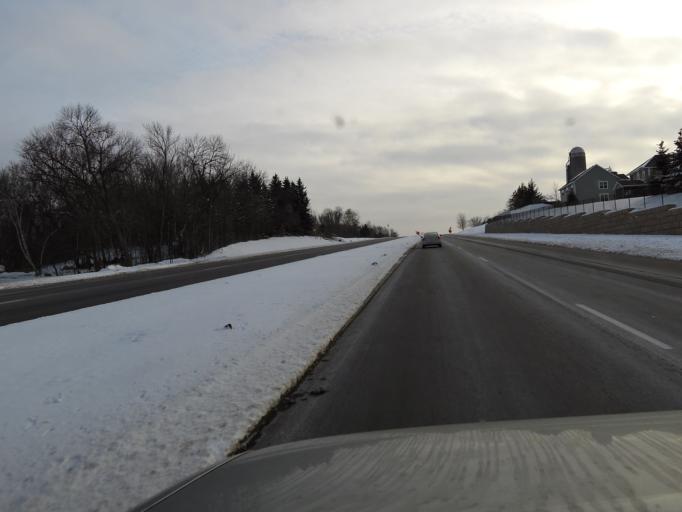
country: US
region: Minnesota
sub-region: Scott County
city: Shakopee
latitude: 44.7650
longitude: -93.5054
